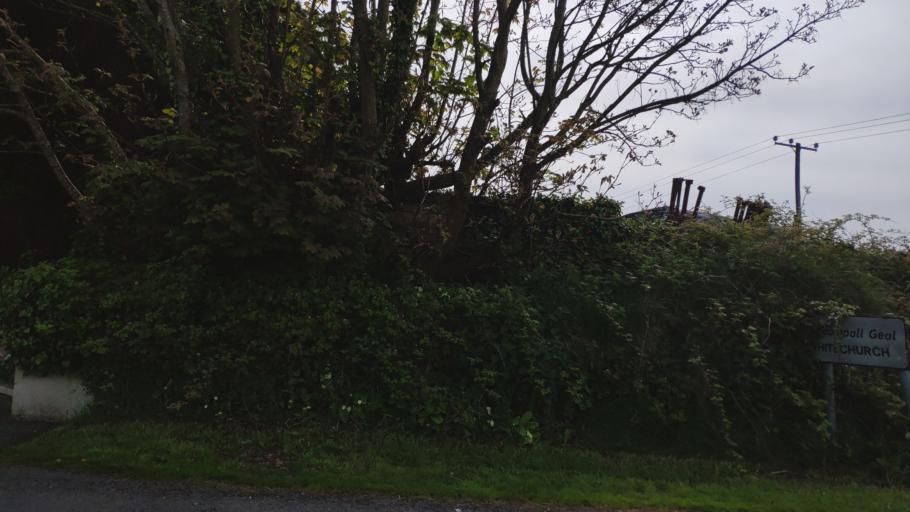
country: IE
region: Munster
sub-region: County Cork
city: Blarney
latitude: 51.9839
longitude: -8.5129
